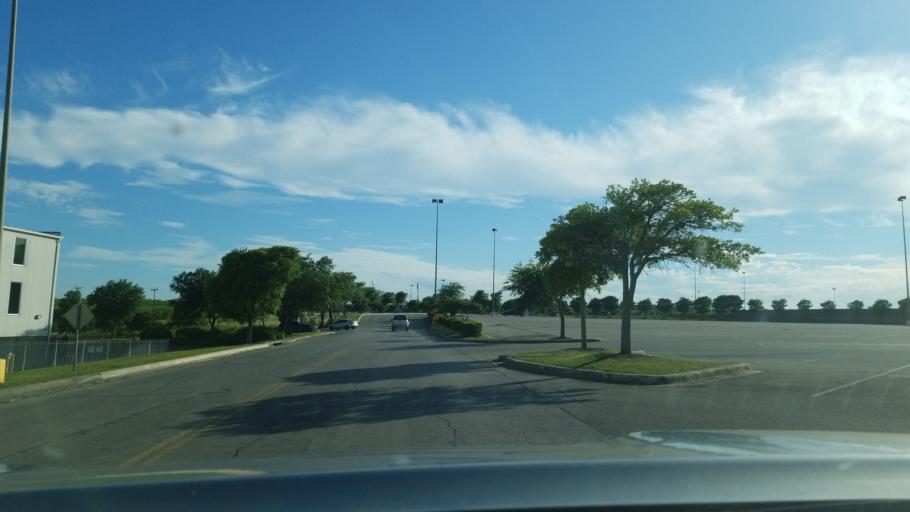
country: US
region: Texas
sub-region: Bexar County
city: Live Oak
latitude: 29.5956
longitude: -98.3469
